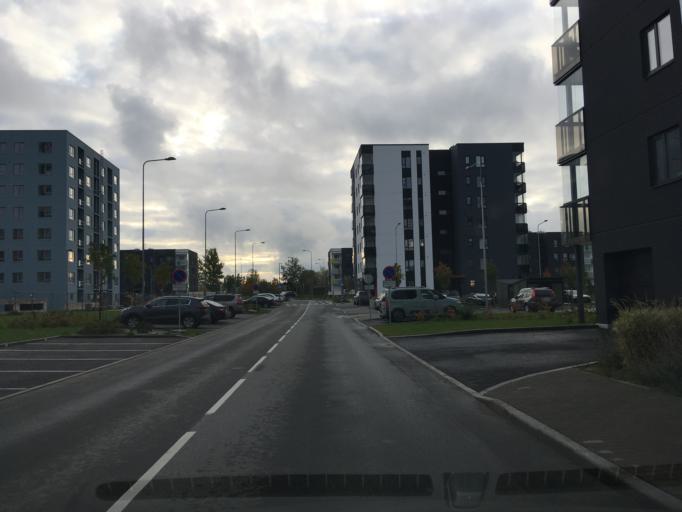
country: EE
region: Harju
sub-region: Tallinna linn
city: Tallinn
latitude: 59.4341
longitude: 24.8095
